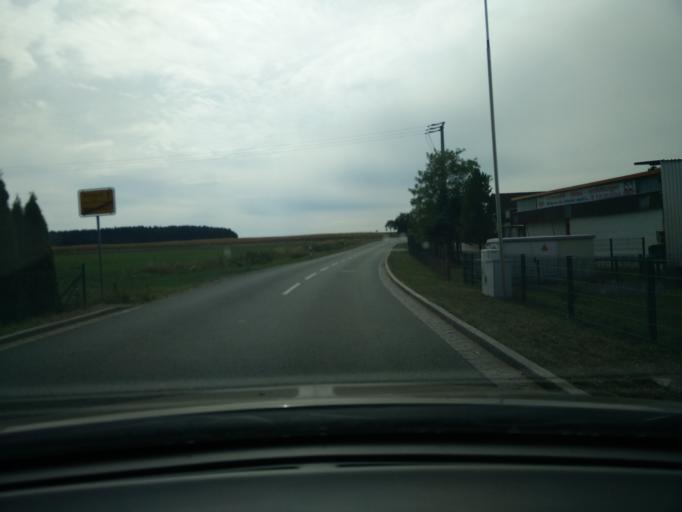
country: DE
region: Bavaria
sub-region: Regierungsbezirk Mittelfranken
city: Hagenbuchach
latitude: 49.5464
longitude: 10.7981
